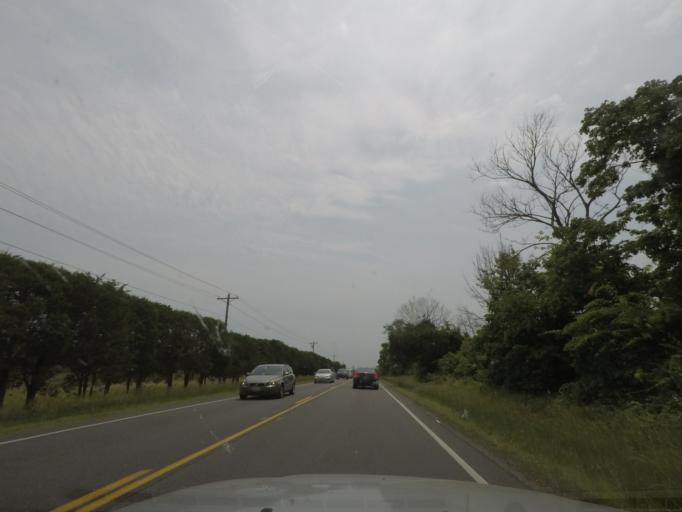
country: US
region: Virginia
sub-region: Prince William County
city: Bull Run Mountain Estates
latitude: 38.9041
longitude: -77.6297
